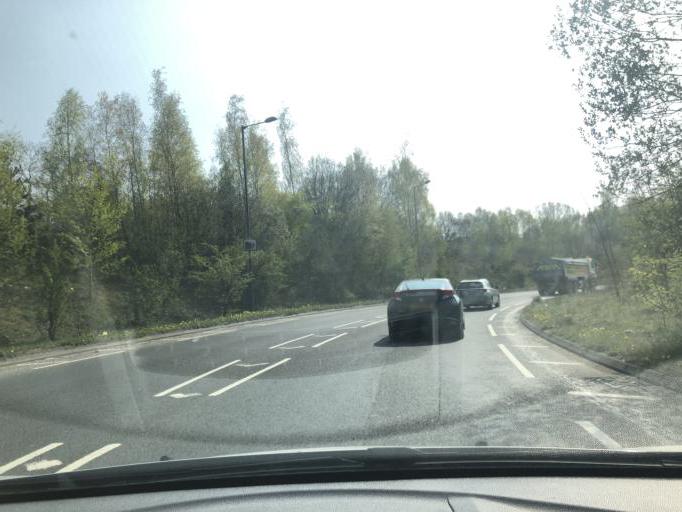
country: GB
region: England
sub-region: Borough of Stockport
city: Bredbury
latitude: 53.4243
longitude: -2.1224
